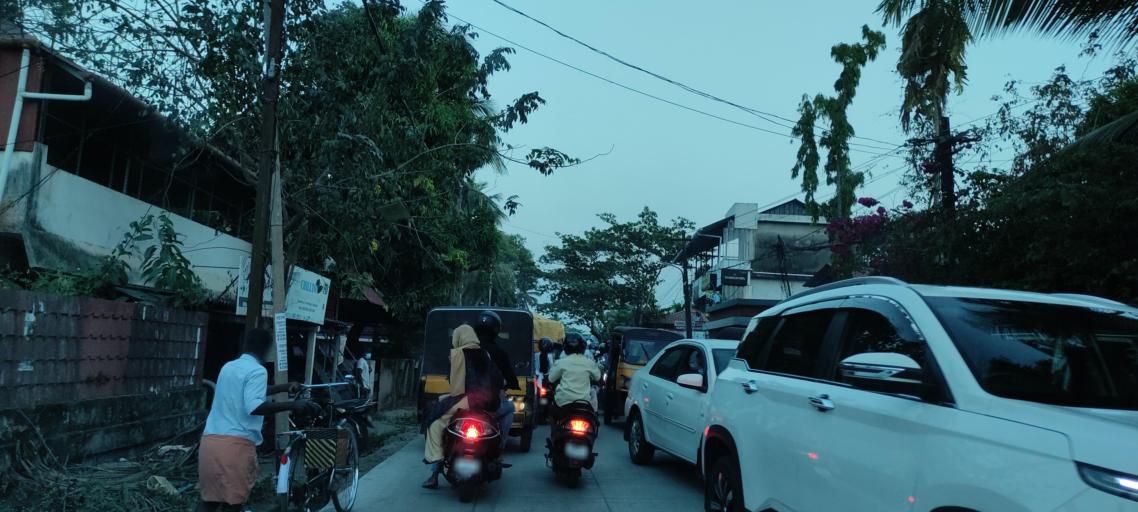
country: IN
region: Kerala
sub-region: Alappuzha
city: Alleppey
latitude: 9.5167
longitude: 76.3343
